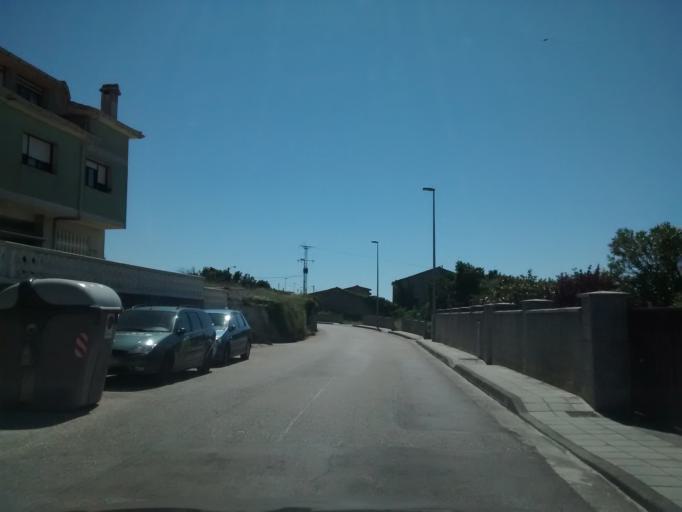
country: ES
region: Cantabria
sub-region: Provincia de Cantabria
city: Santander
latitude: 43.4763
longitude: -3.8209
